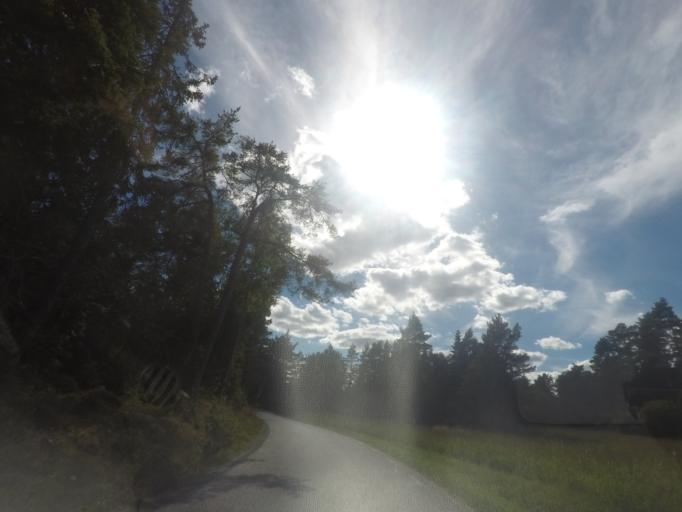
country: SE
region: Stockholm
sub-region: Norrtalje Kommun
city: Arno
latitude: 60.1727
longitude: 18.7356
